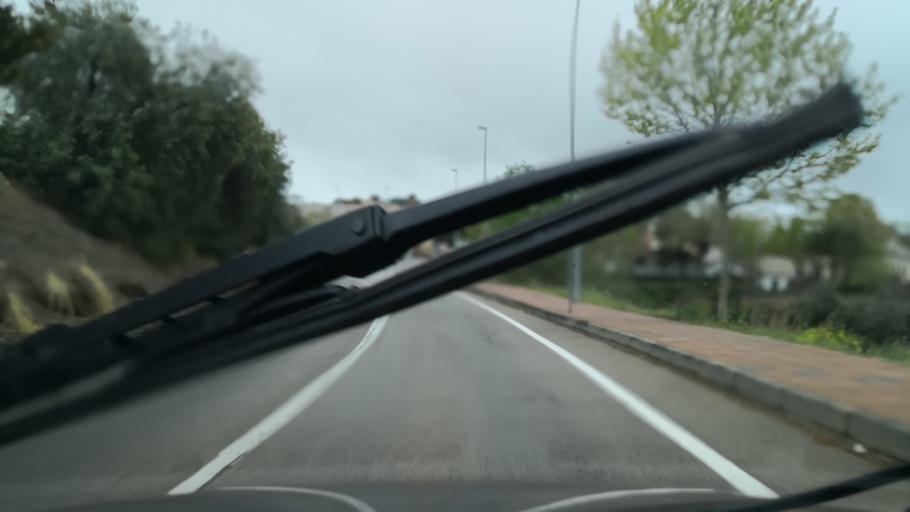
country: ES
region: Extremadura
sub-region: Provincia de Caceres
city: Caceres
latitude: 39.4822
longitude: -6.3801
